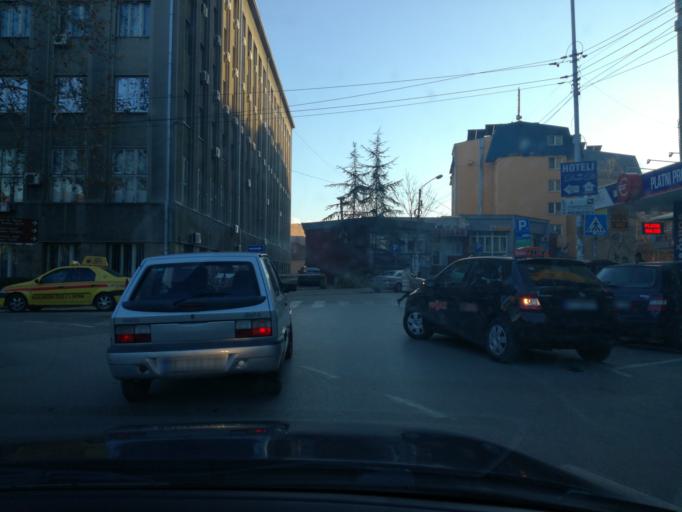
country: RS
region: Central Serbia
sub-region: Nisavski Okrug
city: Nis
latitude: 43.3177
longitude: 21.8904
